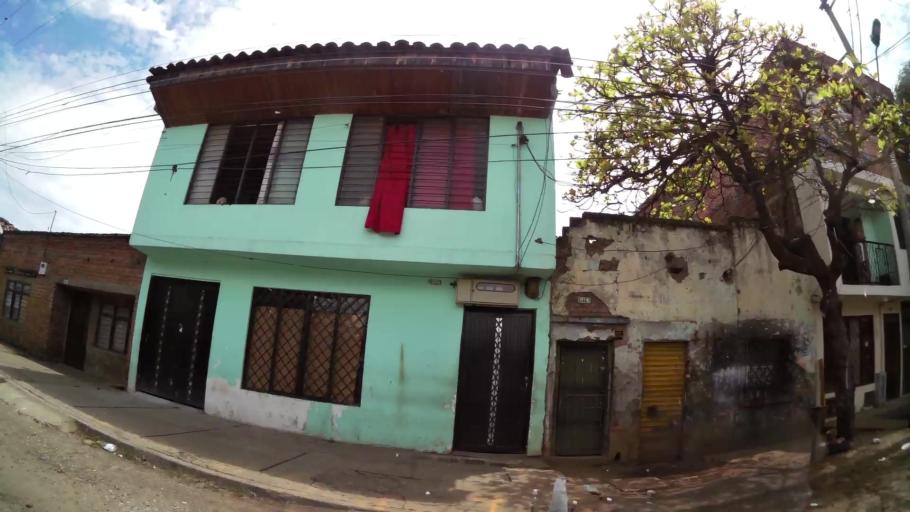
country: CO
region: Valle del Cauca
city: Cali
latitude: 3.4411
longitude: -76.5106
